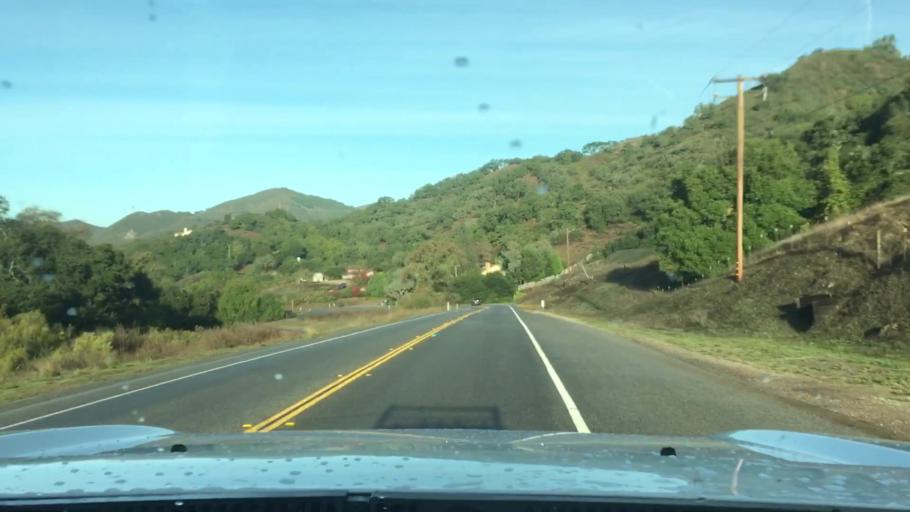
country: US
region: California
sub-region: San Luis Obispo County
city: Atascadero
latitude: 35.4582
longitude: -120.7179
